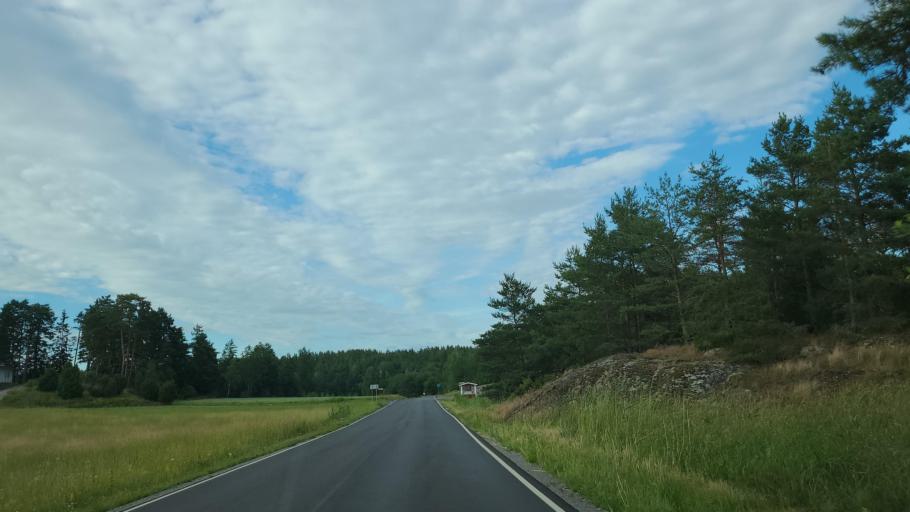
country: FI
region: Varsinais-Suomi
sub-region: Turku
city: Rymaettylae
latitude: 60.3281
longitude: 21.9706
